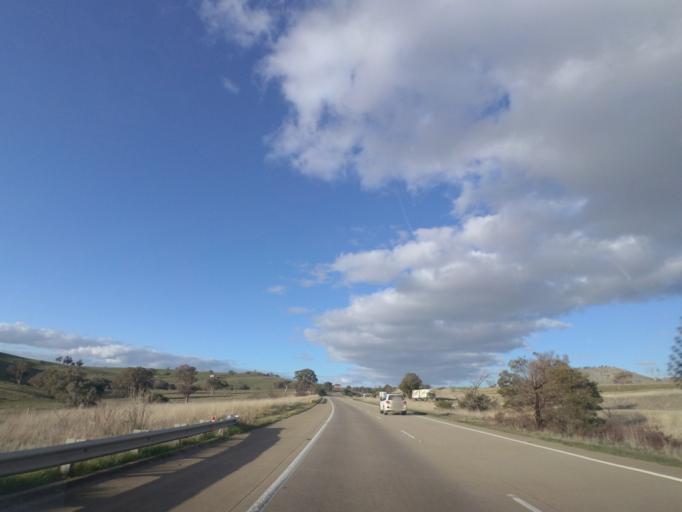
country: AU
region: New South Wales
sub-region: Gundagai
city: Gundagai
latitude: -34.8092
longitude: 148.4629
